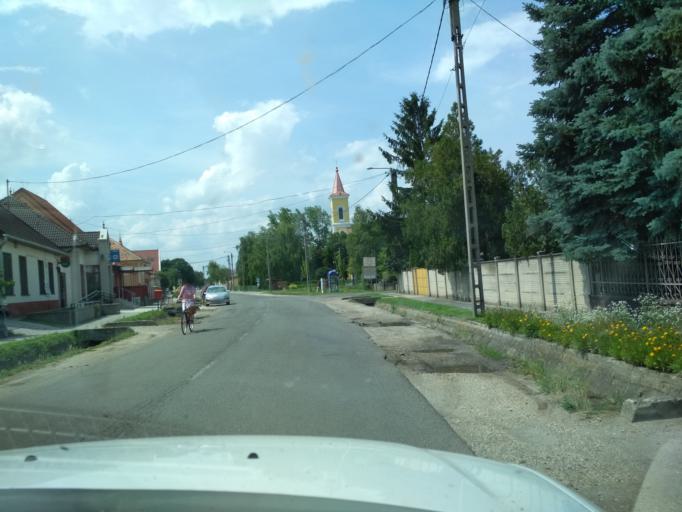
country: HU
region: Pest
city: Tapioszentmarton
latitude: 47.3395
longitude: 19.7494
